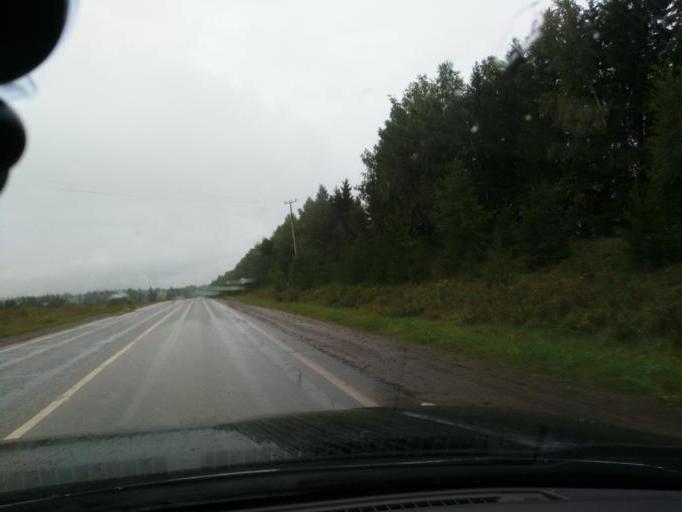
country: RU
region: Perm
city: Osa
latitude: 57.3783
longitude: 55.6095
